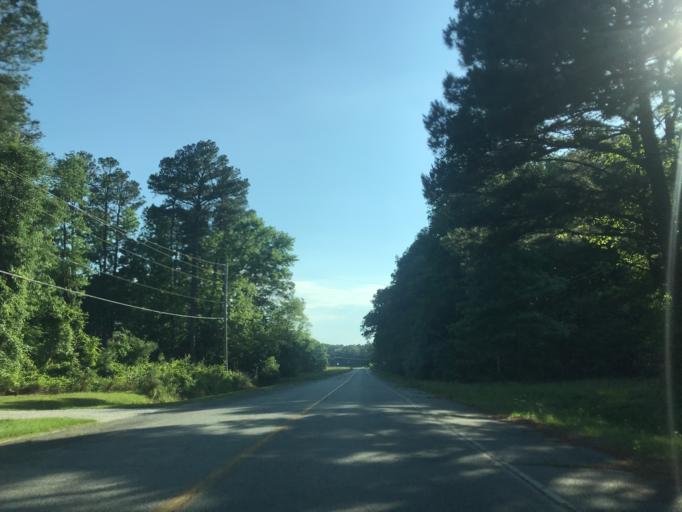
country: US
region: Maryland
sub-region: Wicomico County
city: Hebron
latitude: 38.5341
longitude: -75.7265
